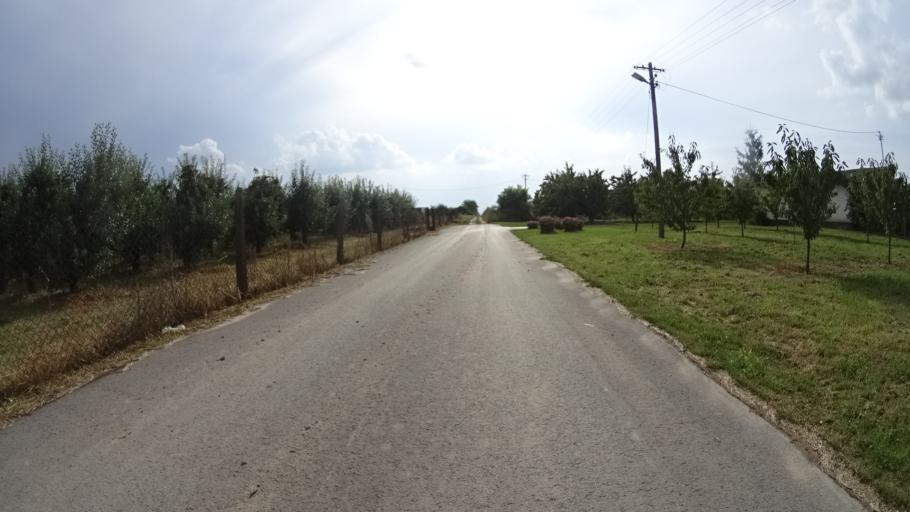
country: PL
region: Masovian Voivodeship
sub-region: Powiat grojecki
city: Goszczyn
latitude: 51.7038
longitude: 20.8377
